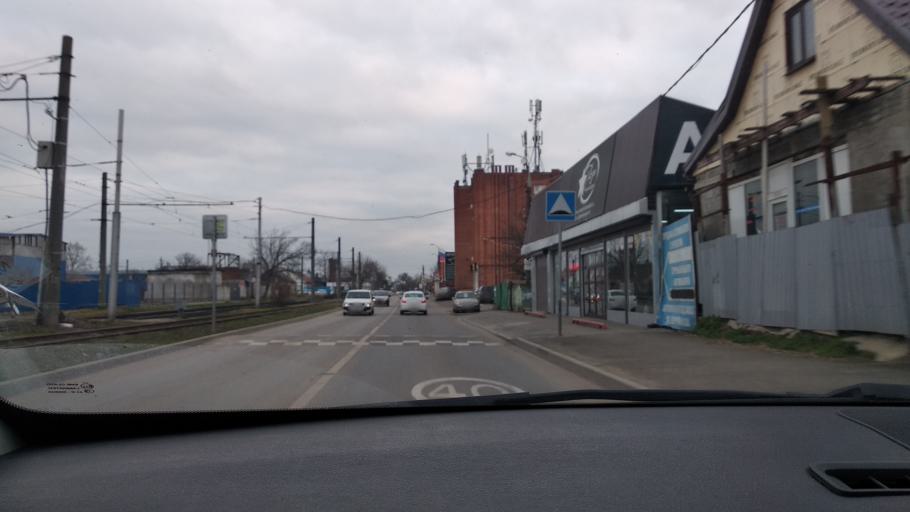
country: RU
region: Krasnodarskiy
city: Krasnodar
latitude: 45.0022
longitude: 39.0217
